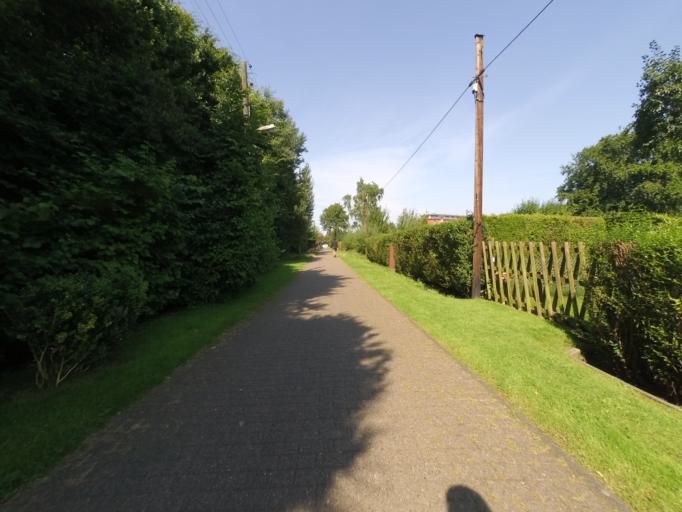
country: DE
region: Hamburg
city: Marienthal
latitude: 53.5479
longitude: 10.0783
